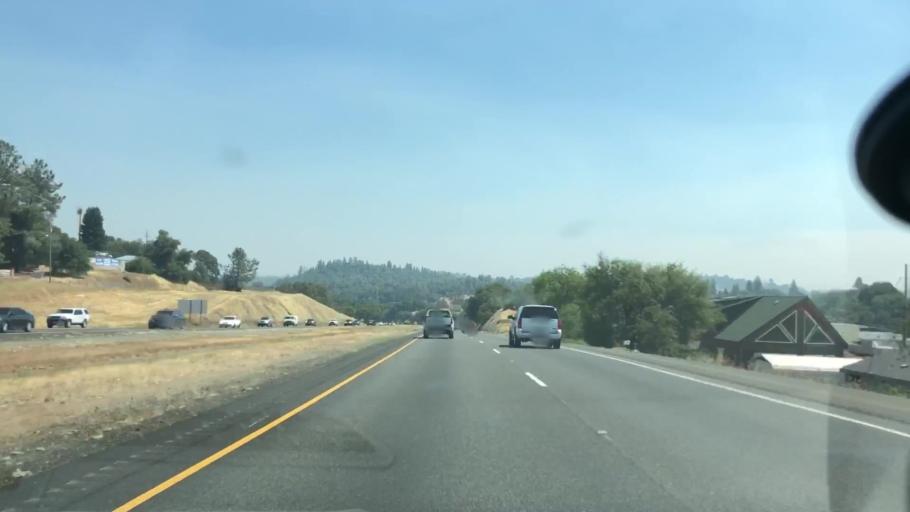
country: US
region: California
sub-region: El Dorado County
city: Shingle Springs
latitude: 38.6637
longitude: -120.9344
